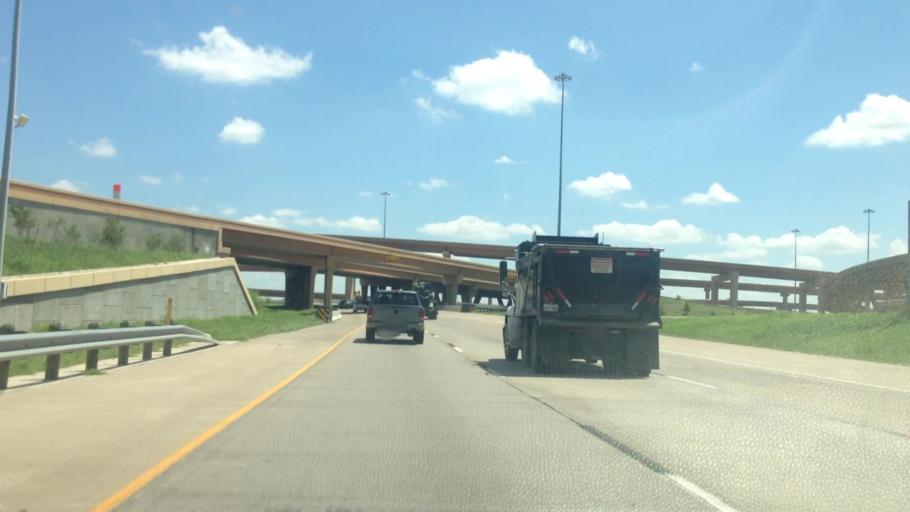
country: US
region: Texas
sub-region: Tarrant County
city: North Richland Hills
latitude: 32.8320
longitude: -97.2090
